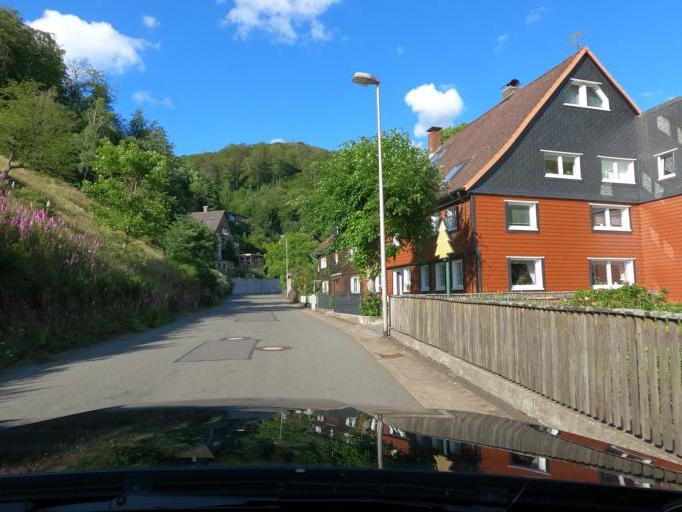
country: DE
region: Lower Saxony
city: Clausthal-Zellerfeld
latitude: 51.7597
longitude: 10.3086
